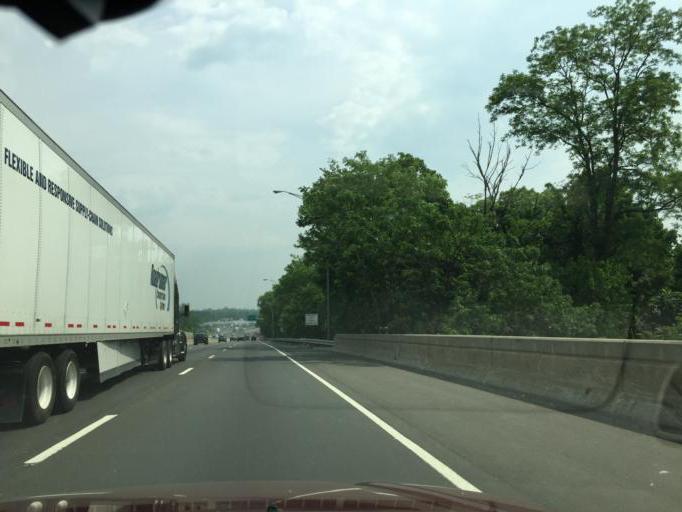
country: US
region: Connecticut
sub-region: Fairfield County
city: Stamford
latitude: 41.0609
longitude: -73.5102
